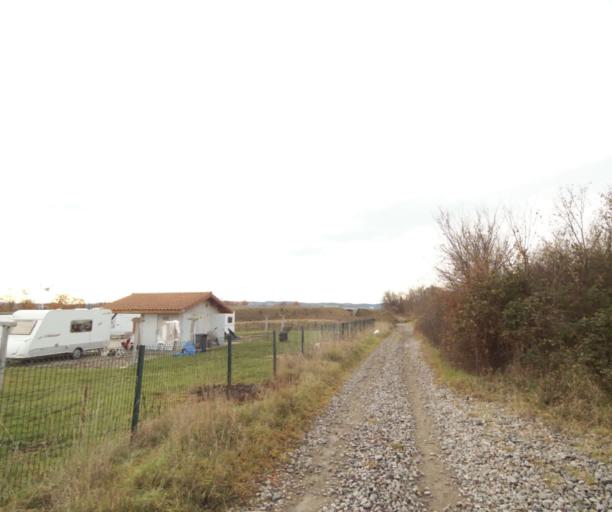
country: FR
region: Rhone-Alpes
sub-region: Departement de la Loire
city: Sury-le-Comtal
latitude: 45.5264
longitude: 4.1949
